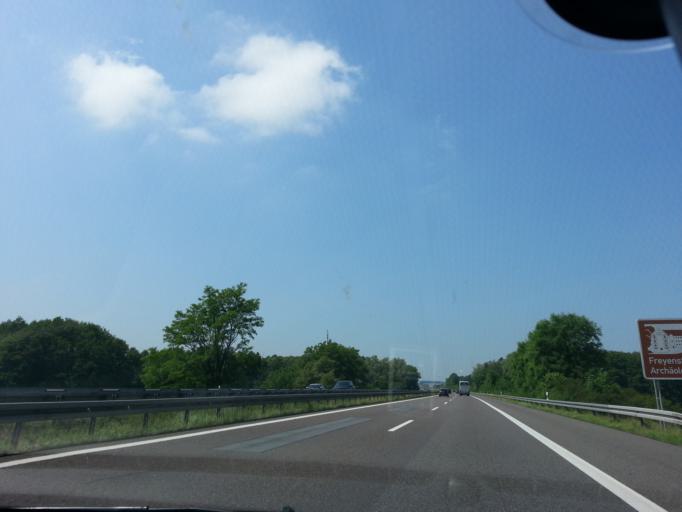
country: DE
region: Brandenburg
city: Gerdshagen
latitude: 53.2002
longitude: 12.2710
